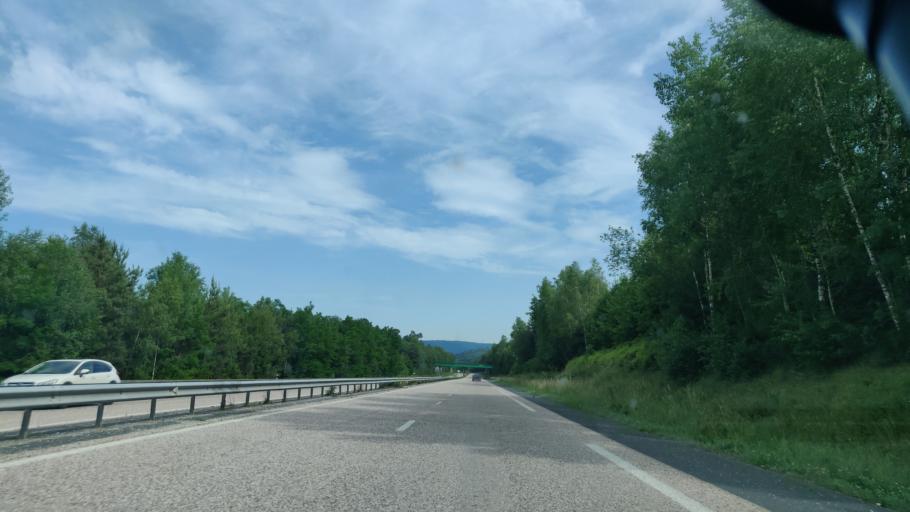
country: FR
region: Lorraine
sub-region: Departement de Meurthe-et-Moselle
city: Baccarat
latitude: 48.4452
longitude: 6.7569
